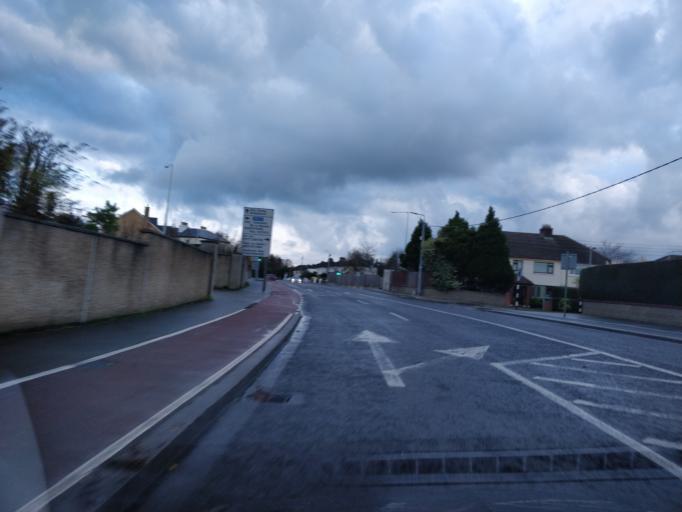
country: IE
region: Leinster
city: Sandyford
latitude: 53.2864
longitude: -6.2245
